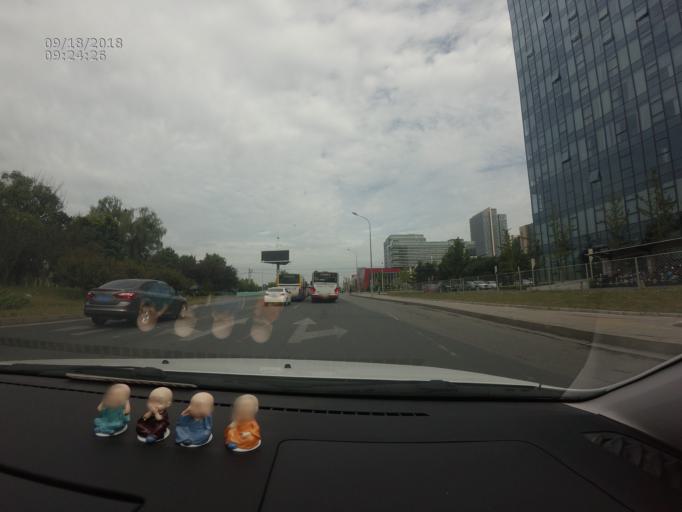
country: CN
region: Beijing
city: Xibeiwang
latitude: 40.0714
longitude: 116.2387
